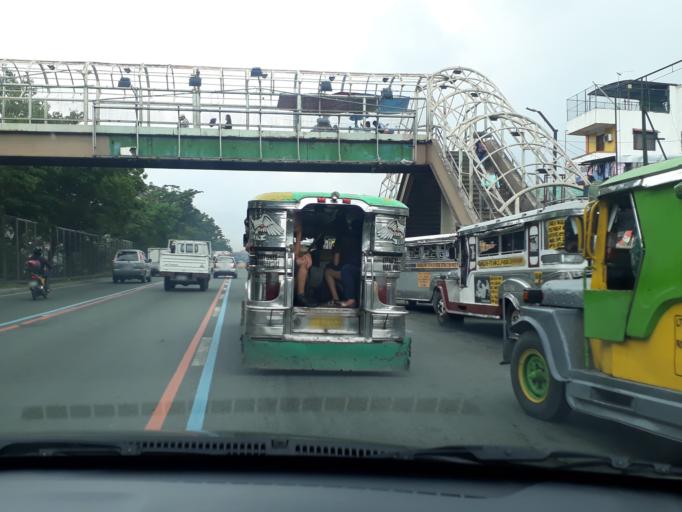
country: PH
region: Calabarzon
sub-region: Province of Rizal
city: Pateros
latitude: 14.5280
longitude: 121.0564
